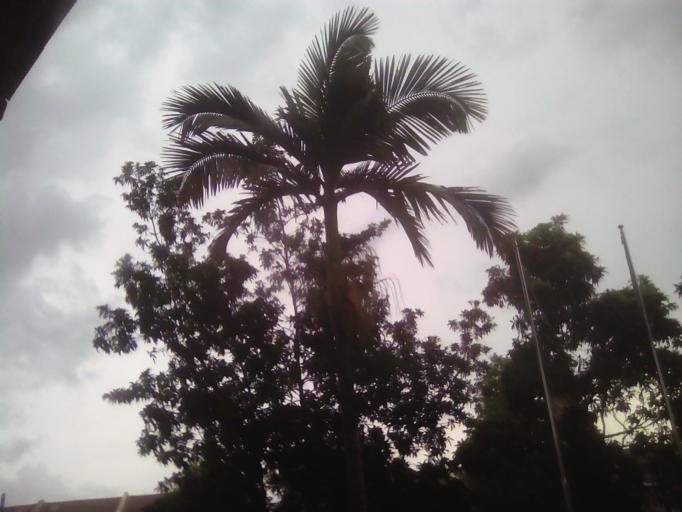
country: MY
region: Penang
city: Butterworth
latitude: 5.4060
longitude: 100.3822
